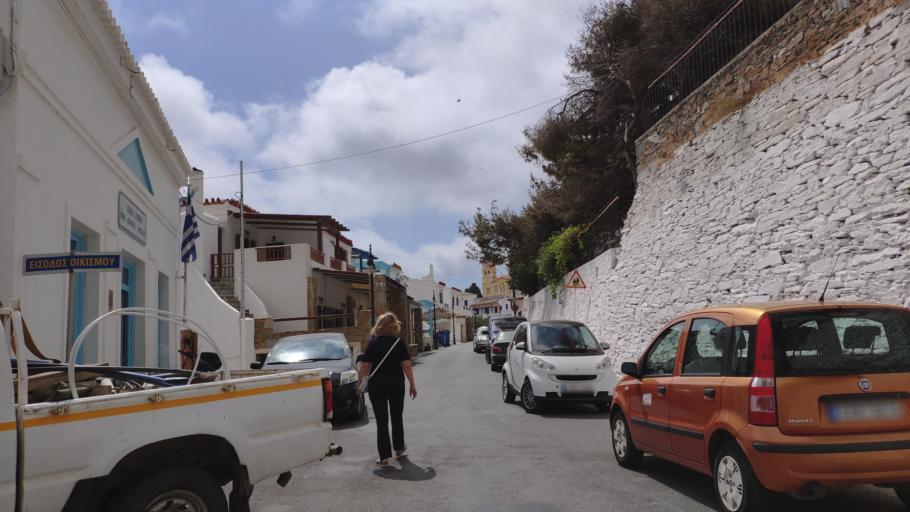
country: GR
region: South Aegean
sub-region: Nomos Kykladon
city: Kythnos
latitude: 37.3834
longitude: 24.4322
